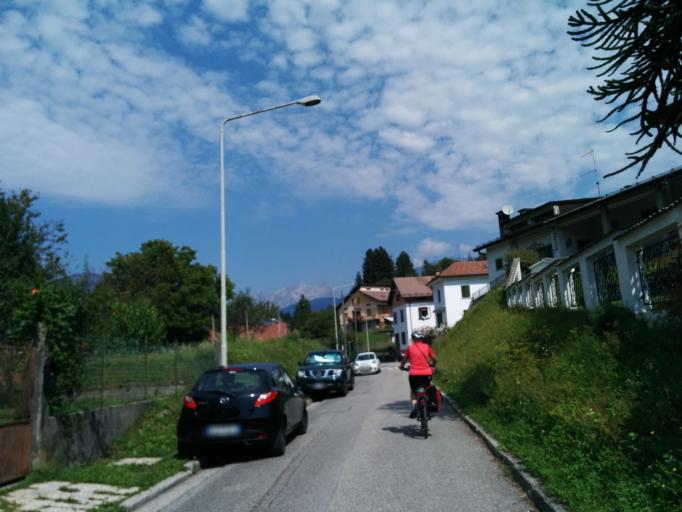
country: IT
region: Friuli Venezia Giulia
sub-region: Provincia di Udine
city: Ovaro
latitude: 46.4807
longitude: 12.8679
